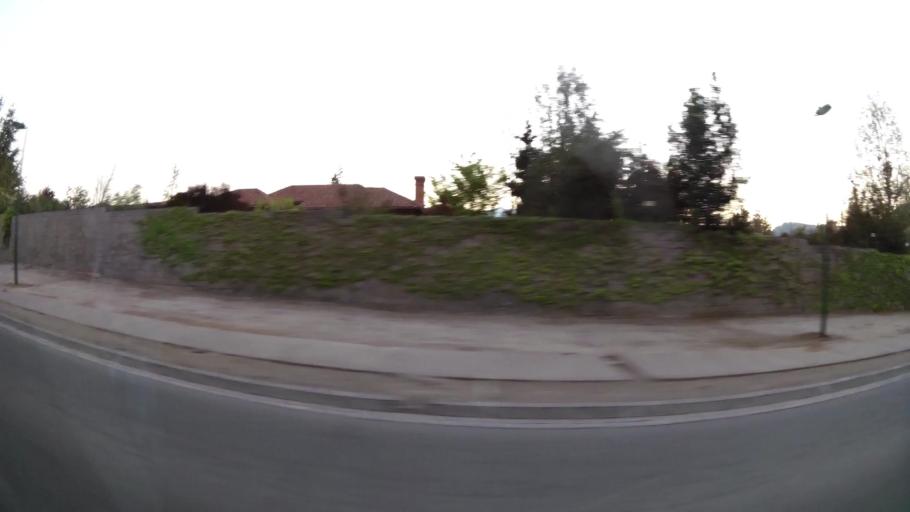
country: CL
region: Santiago Metropolitan
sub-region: Provincia de Chacabuco
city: Chicureo Abajo
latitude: -33.3227
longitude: -70.5430
